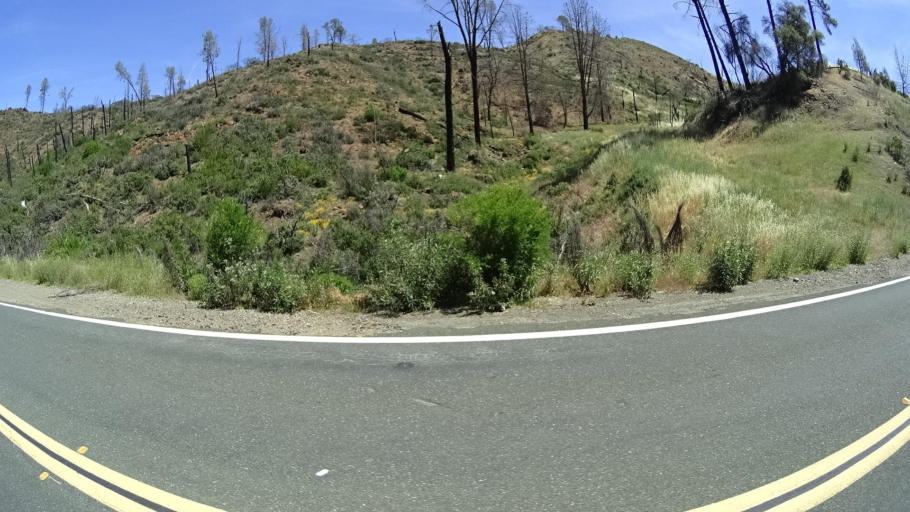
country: US
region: California
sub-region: Lake County
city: Hidden Valley Lake
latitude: 38.7160
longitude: -122.4880
